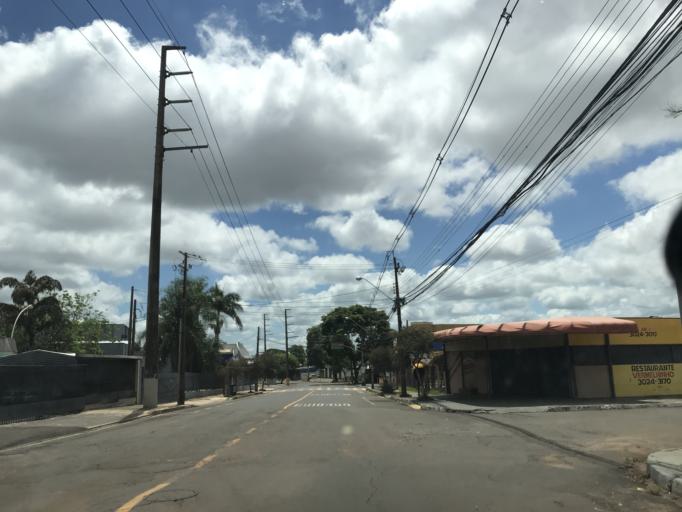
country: BR
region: Parana
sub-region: Londrina
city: Londrina
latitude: -23.2956
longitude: -51.1665
